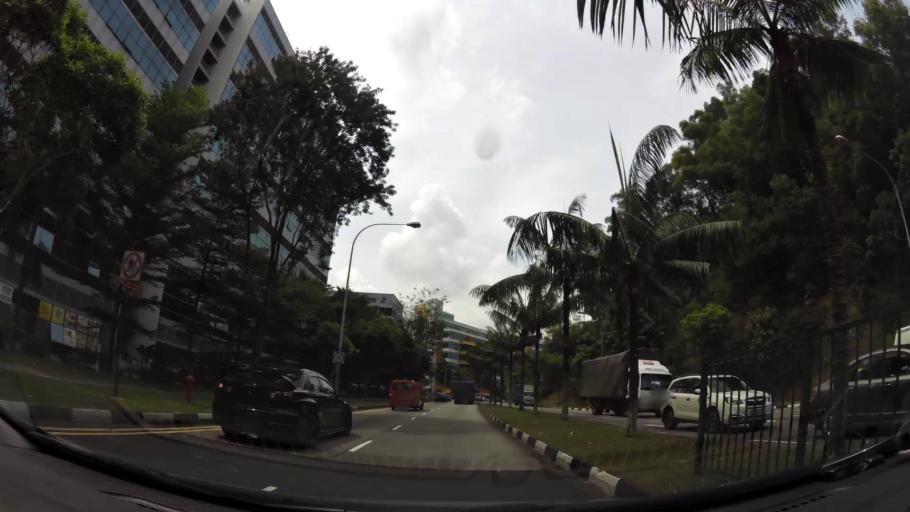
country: SG
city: Singapore
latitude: 1.3400
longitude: 103.7593
